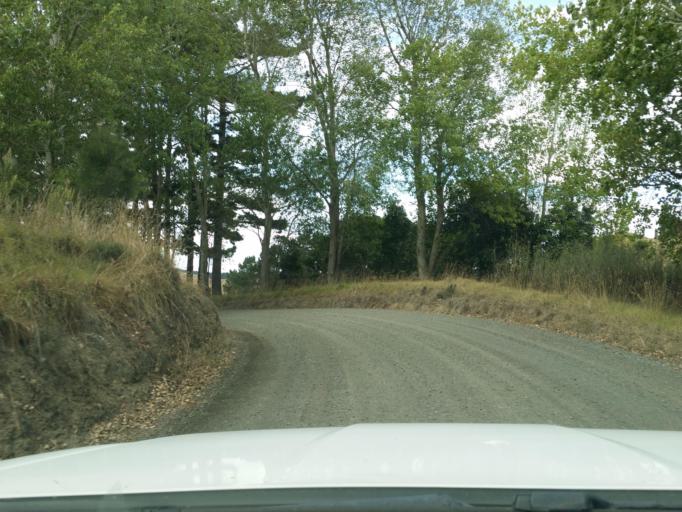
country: NZ
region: Auckland
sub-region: Auckland
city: Wellsford
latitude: -36.3271
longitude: 174.1423
